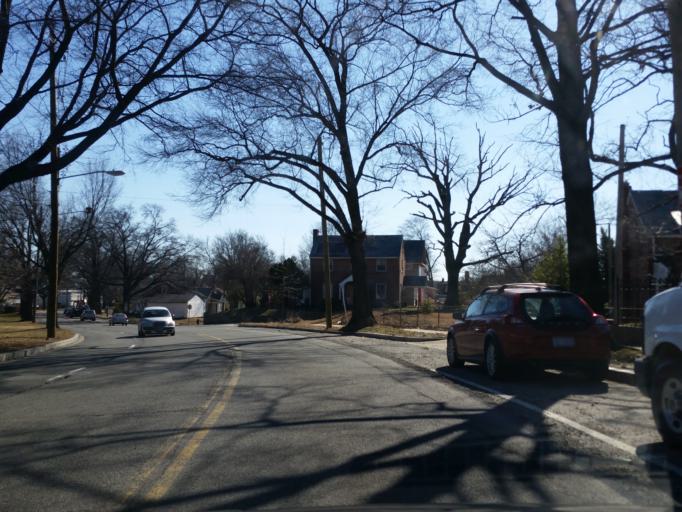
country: US
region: Maryland
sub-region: Montgomery County
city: Takoma Park
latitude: 38.9679
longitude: -77.0141
